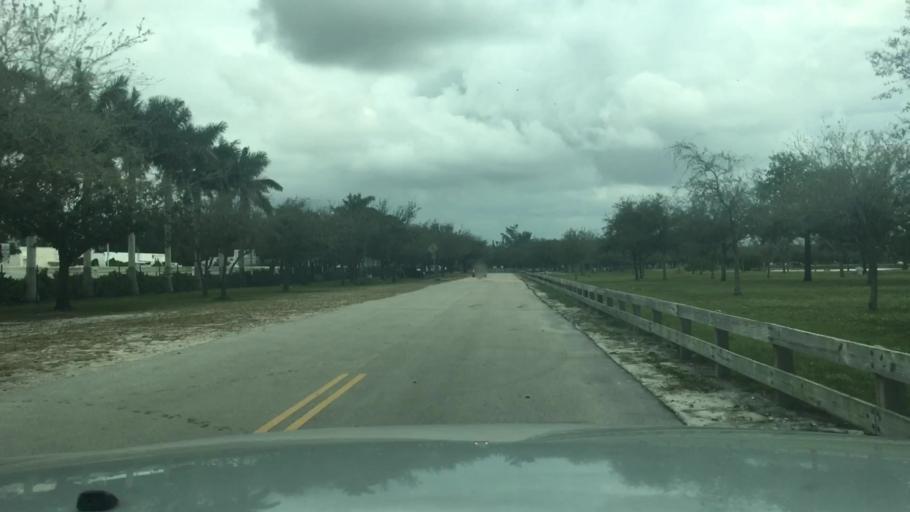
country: US
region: Florida
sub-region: Miami-Dade County
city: Opa-locka
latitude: 25.8911
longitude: -80.2776
